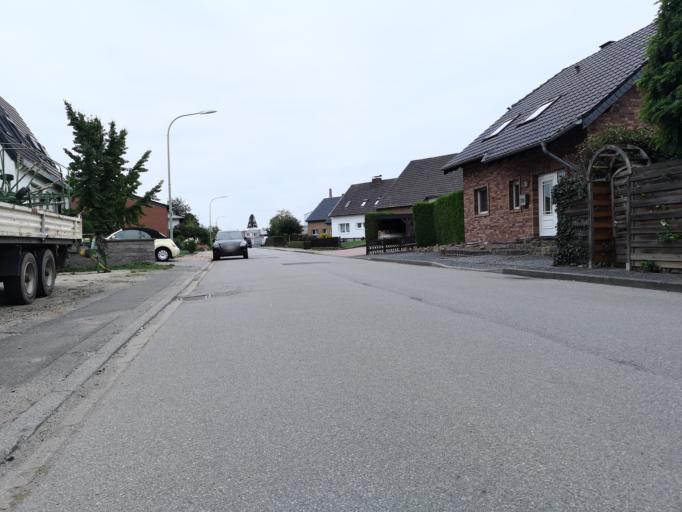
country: DE
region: North Rhine-Westphalia
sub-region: Regierungsbezirk Koln
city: Kreuzau
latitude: 50.7492
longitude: 6.4947
